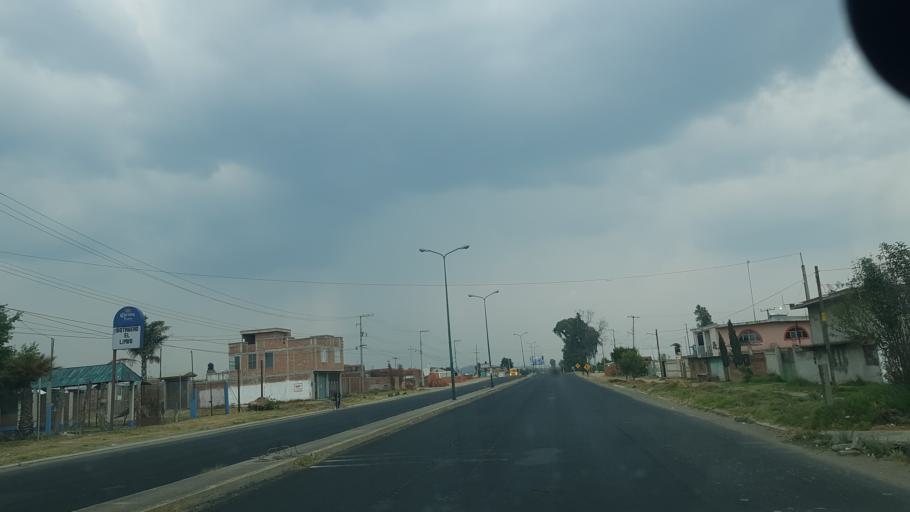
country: MX
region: Puebla
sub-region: Huejotzingo
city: San Mateo Capultitlan
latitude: 19.1798
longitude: -98.4161
